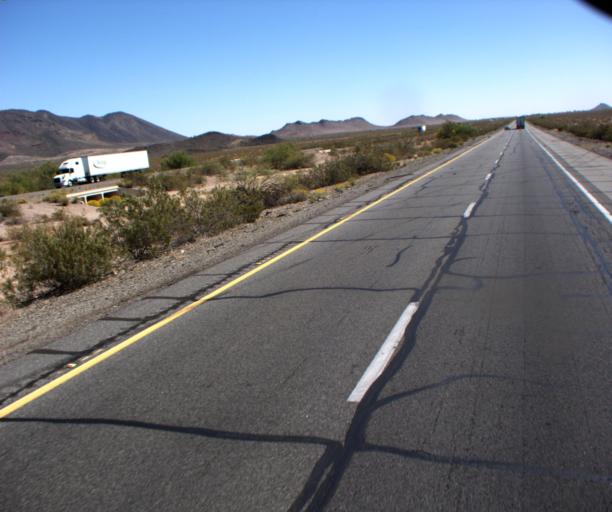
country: US
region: Arizona
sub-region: Maricopa County
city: Buckeye
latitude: 33.5260
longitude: -113.1035
